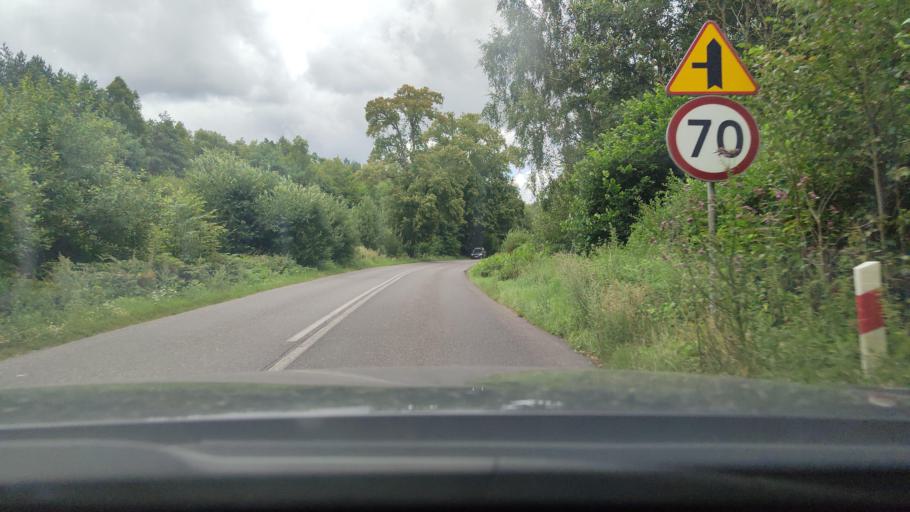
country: PL
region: Pomeranian Voivodeship
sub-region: Powiat pucki
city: Krokowa
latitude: 54.7335
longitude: 18.1642
